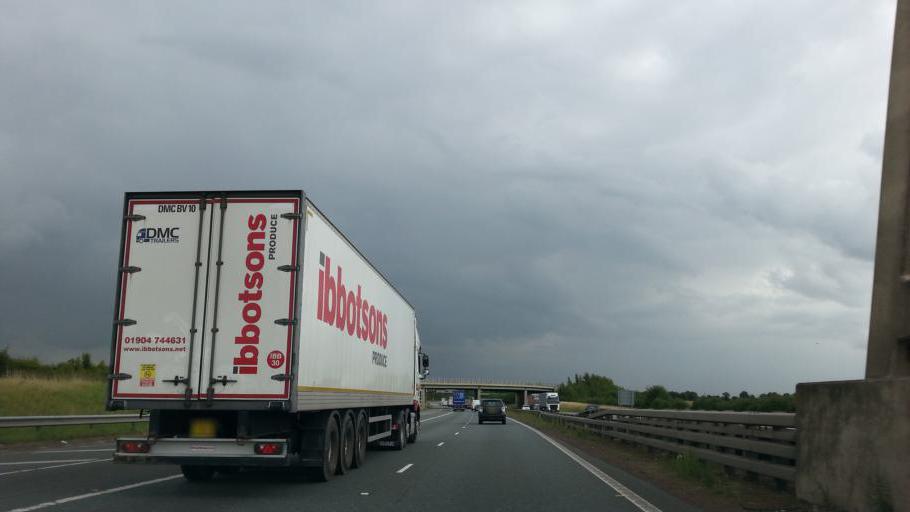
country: GB
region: England
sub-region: City and Borough of Wakefield
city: Darrington
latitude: 53.6877
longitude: -1.2697
